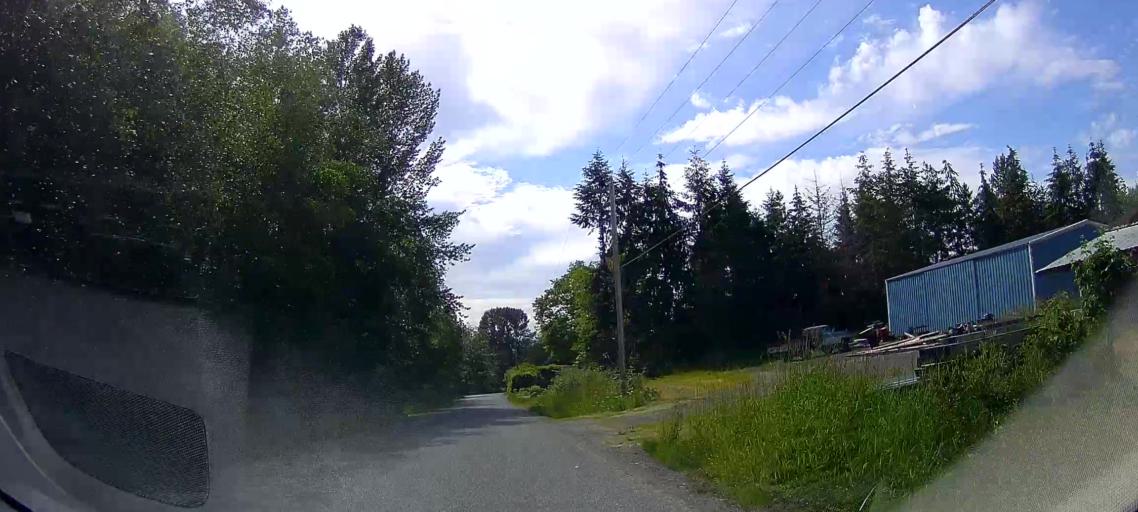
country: US
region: Washington
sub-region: Skagit County
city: Burlington
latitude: 48.5448
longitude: -122.3769
